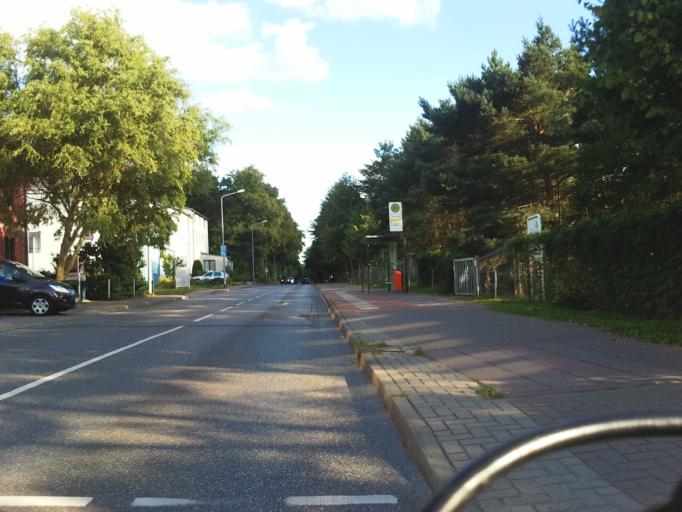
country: DE
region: Mecklenburg-Vorpommern
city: Rostock
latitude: 54.1010
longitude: 12.1199
